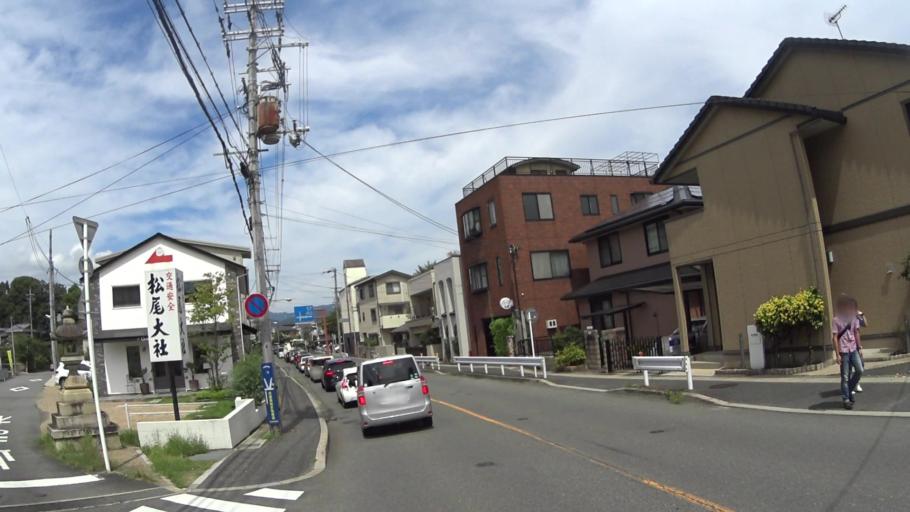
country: JP
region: Kyoto
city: Muko
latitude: 34.9992
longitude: 135.6882
